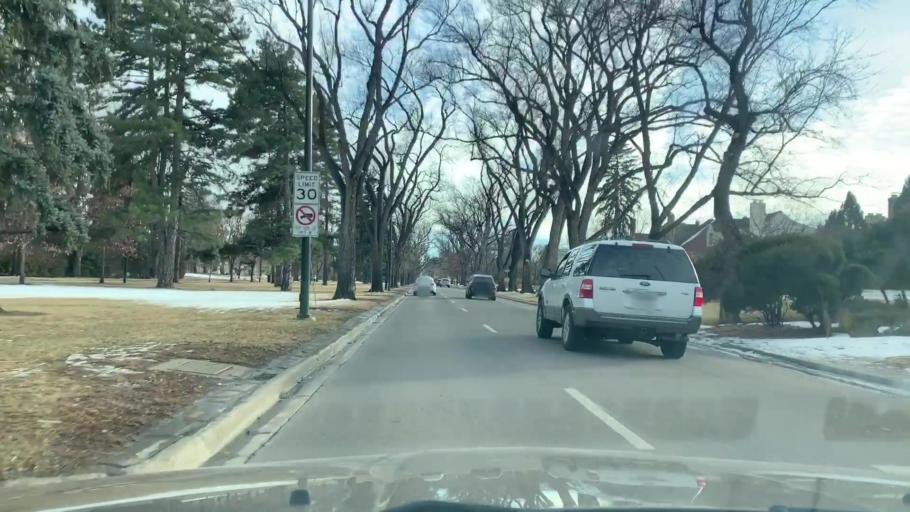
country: US
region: Colorado
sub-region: Arapahoe County
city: Glendale
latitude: 39.7291
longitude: -104.9128
